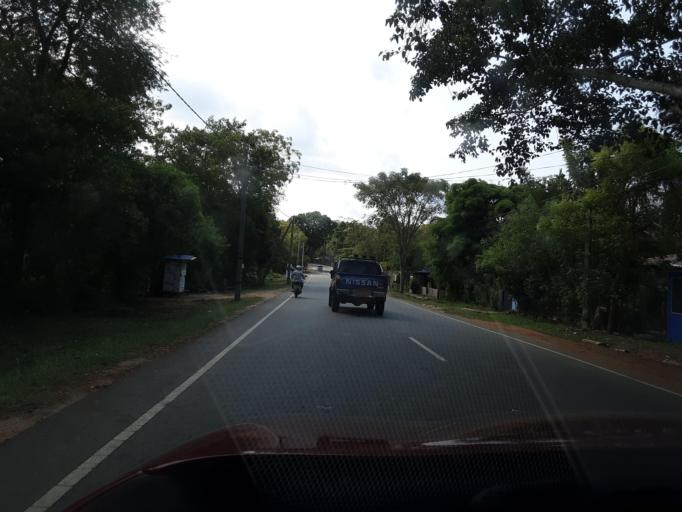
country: LK
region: Uva
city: Haputale
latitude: 6.3542
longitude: 81.1922
